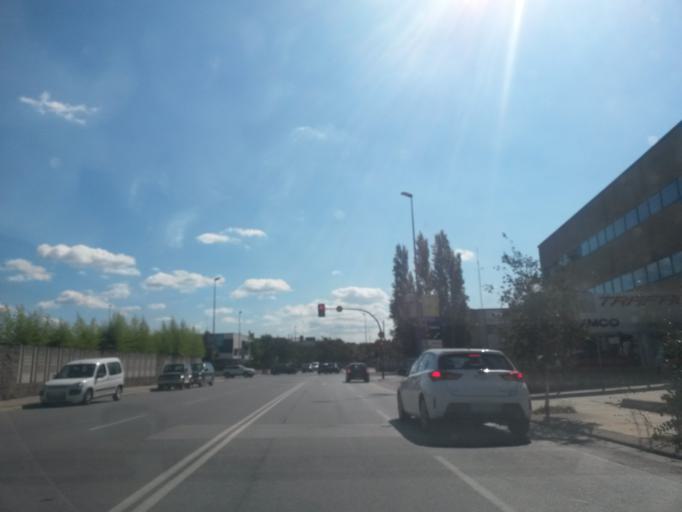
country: ES
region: Catalonia
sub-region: Provincia de Girona
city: Salt
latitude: 41.9670
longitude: 2.8047
